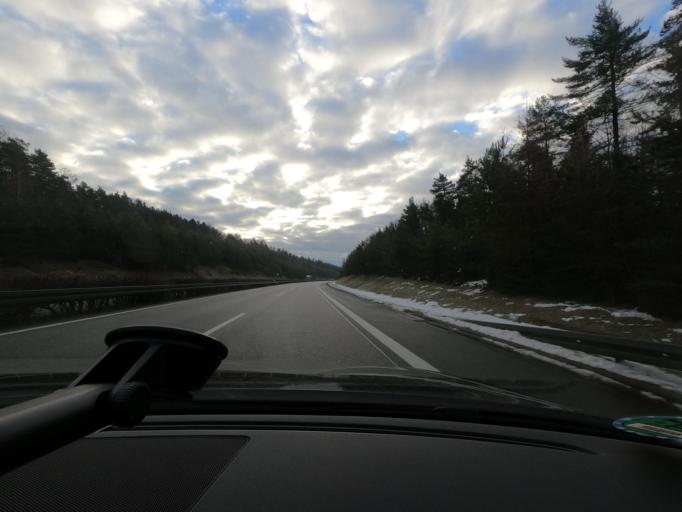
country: DE
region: Thuringia
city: Eisfeld
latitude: 50.3986
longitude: 10.9139
